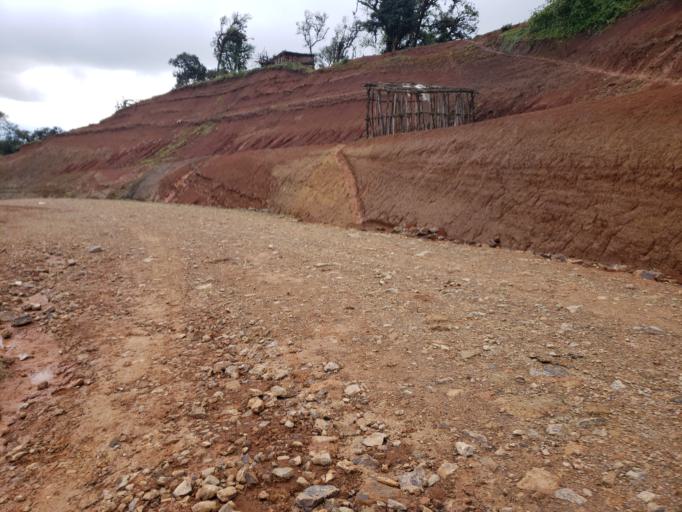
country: ET
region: Oromiya
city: Dodola
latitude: 6.6767
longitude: 39.3641
